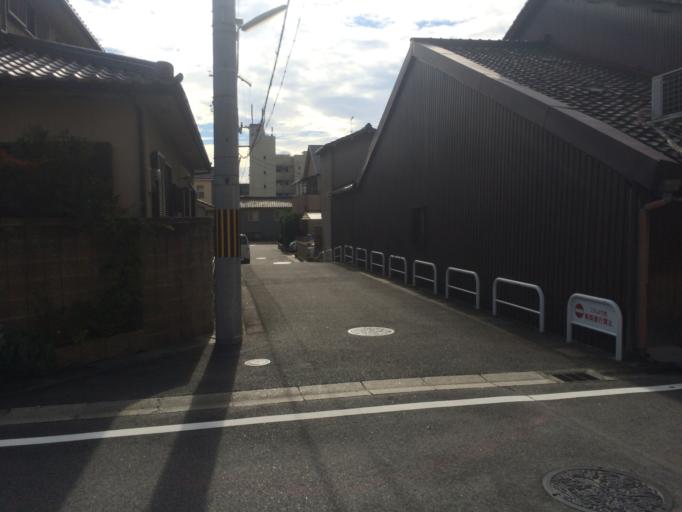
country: JP
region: Nara
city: Nara-shi
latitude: 34.6733
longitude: 135.8306
